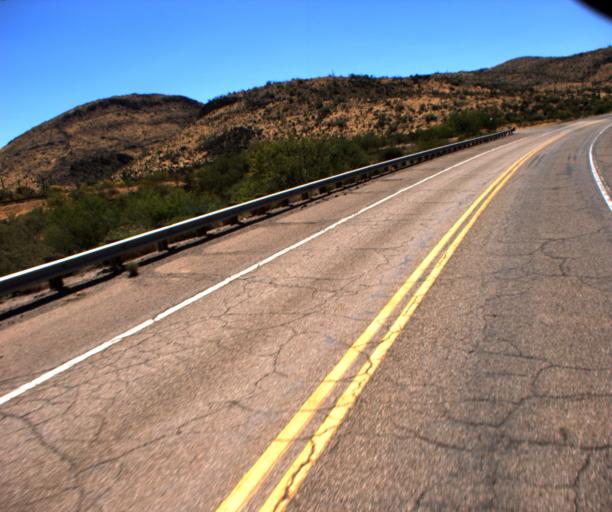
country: US
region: Arizona
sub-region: Pinal County
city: Superior
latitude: 33.2489
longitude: -111.0967
